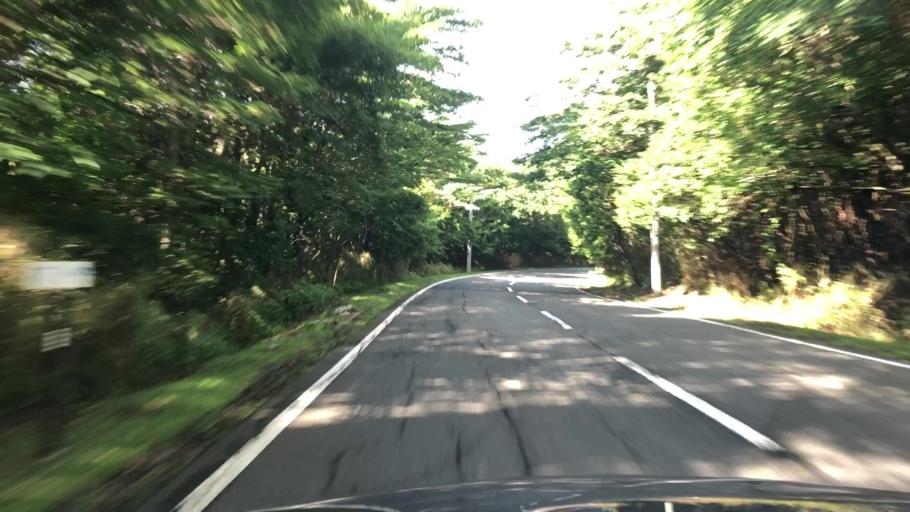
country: JP
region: Shizuoka
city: Gotemba
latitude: 35.3198
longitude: 138.7911
